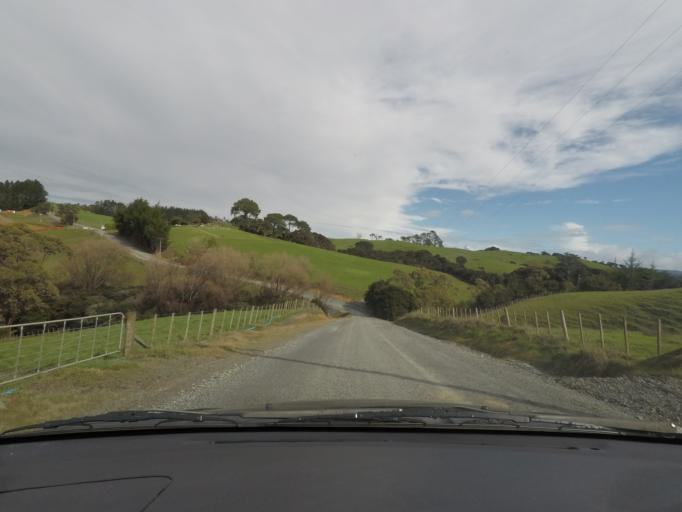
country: NZ
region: Auckland
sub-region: Auckland
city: Warkworth
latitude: -36.4486
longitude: 174.7505
